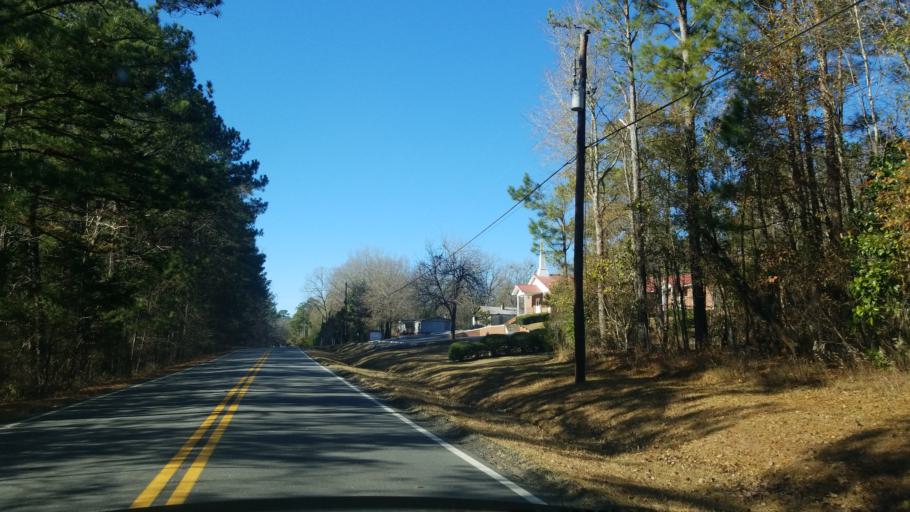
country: US
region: Georgia
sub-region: Harris County
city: Hamilton
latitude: 32.6664
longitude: -84.8733
